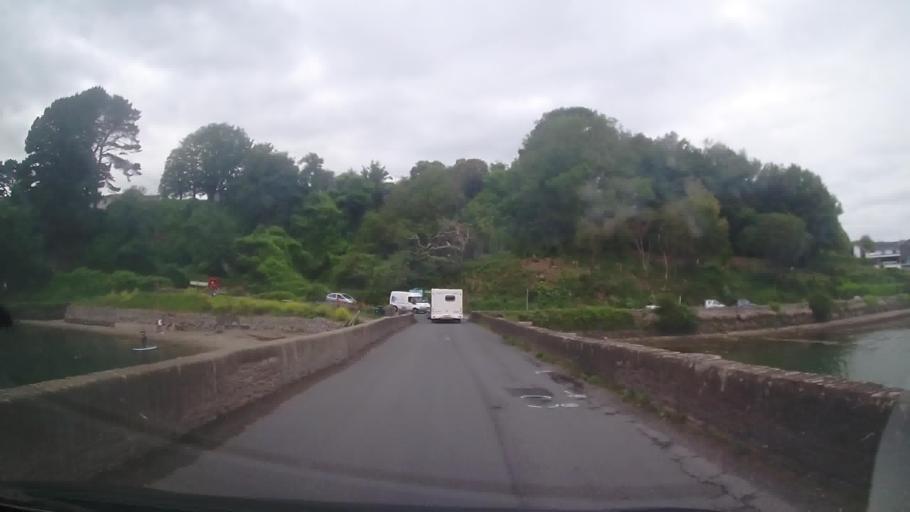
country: GB
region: England
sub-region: Devon
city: Kingsbridge
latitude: 50.2749
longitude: -3.7624
